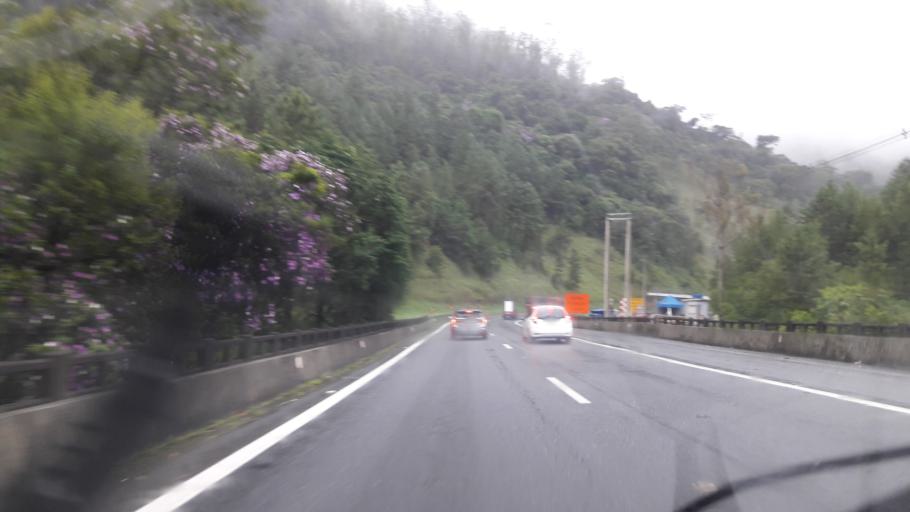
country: BR
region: Sao Paulo
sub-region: Juquitiba
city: Juquitiba
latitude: -24.0546
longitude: -47.2163
